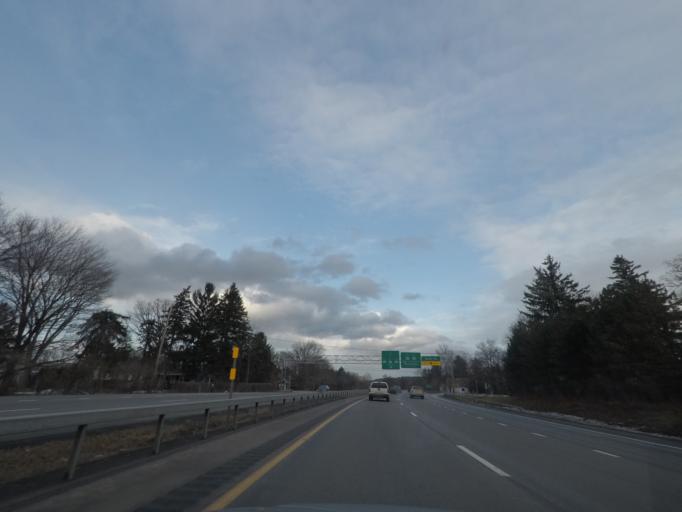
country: US
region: New York
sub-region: Oneida County
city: New Hartford
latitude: 43.0793
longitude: -75.3005
